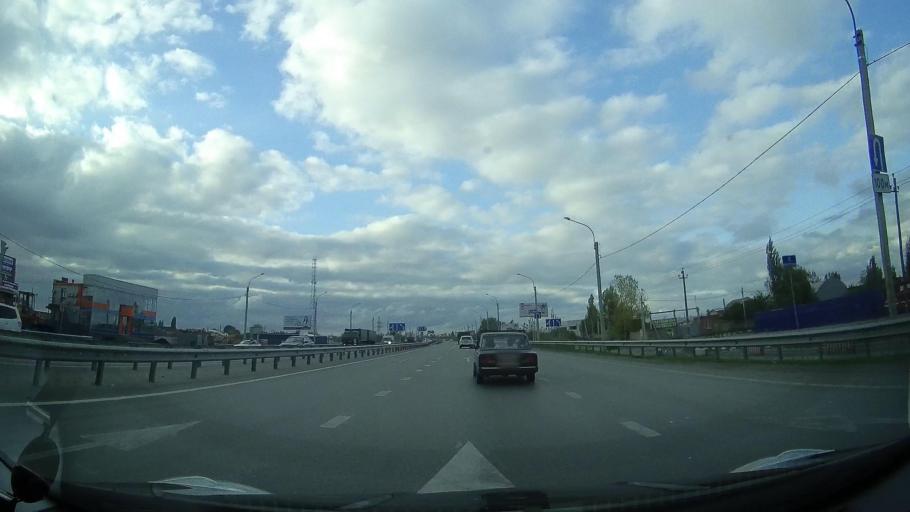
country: RU
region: Rostov
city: Bataysk
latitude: 47.1555
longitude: 39.7694
